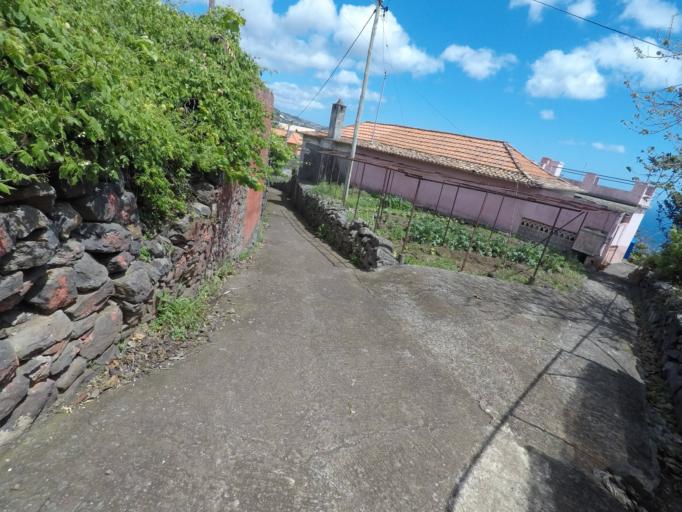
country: PT
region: Madeira
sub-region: Calheta
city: Estreito da Calheta
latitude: 32.7384
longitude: -17.1941
